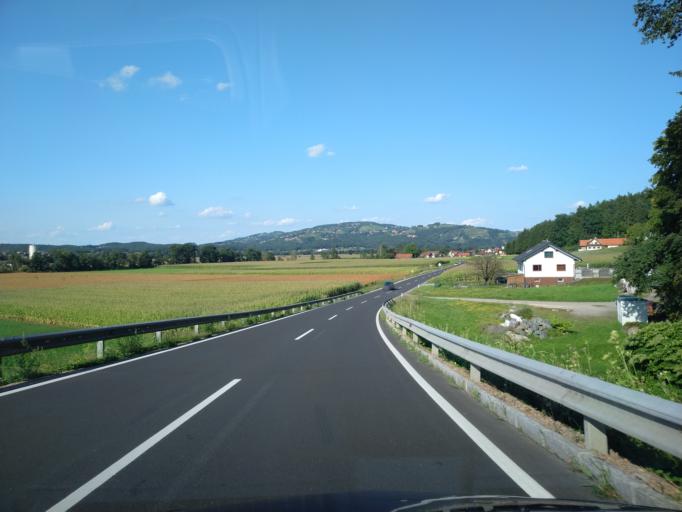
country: AT
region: Styria
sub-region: Politischer Bezirk Leibnitz
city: Gleinstatten
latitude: 46.7436
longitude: 15.3679
